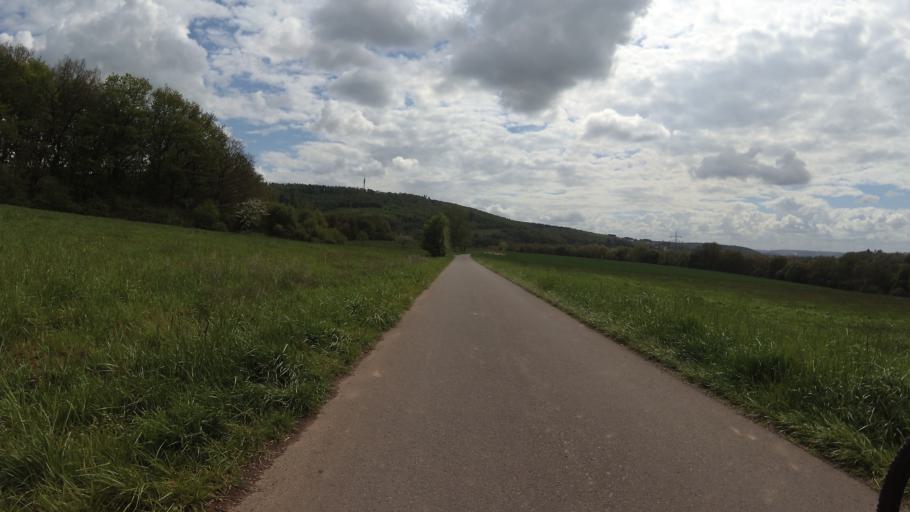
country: DE
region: Saarland
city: Schmelz
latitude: 49.4028
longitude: 6.8585
